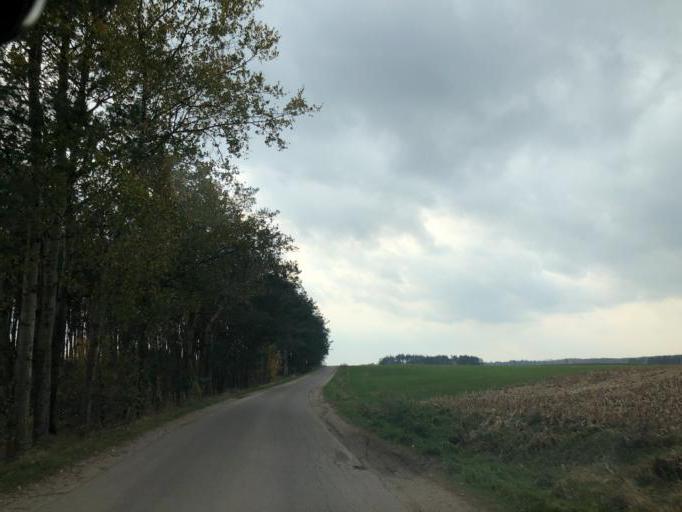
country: PL
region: Podlasie
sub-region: Lomza
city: Lomza
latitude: 53.1493
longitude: 21.9949
